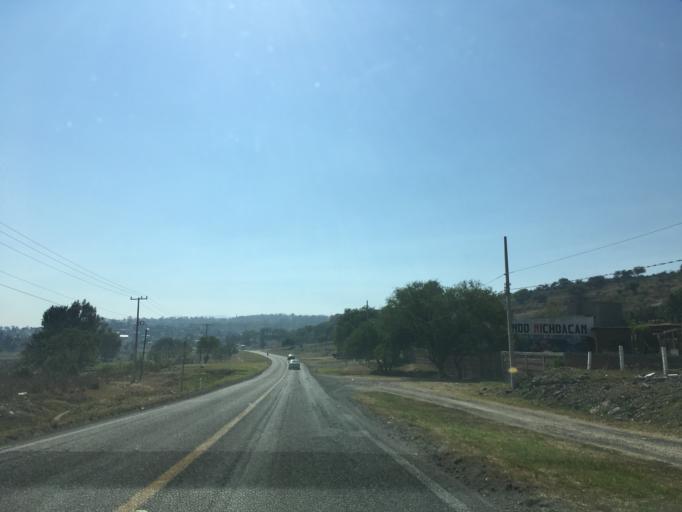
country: MX
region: Michoacan
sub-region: Morelia
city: Fraccionamiento Mision del Valle
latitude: 19.7360
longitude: -101.0913
